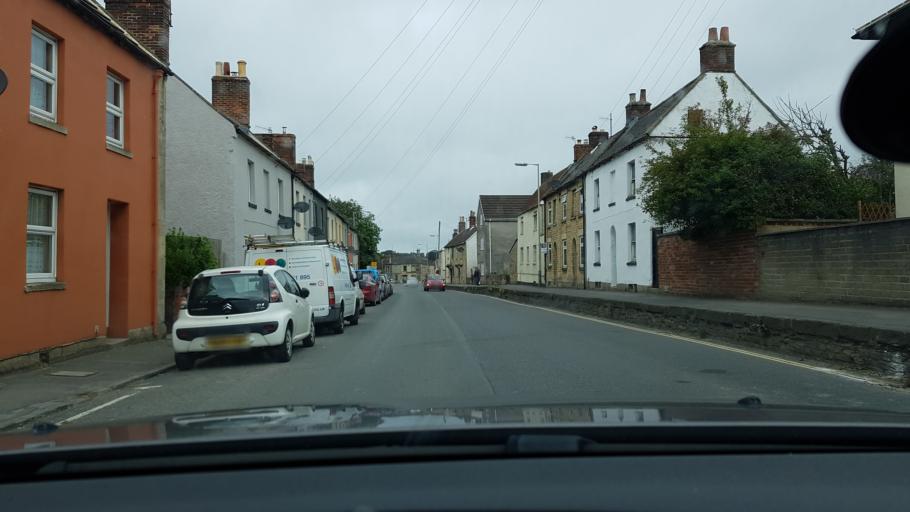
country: GB
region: England
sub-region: Wiltshire
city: Calne
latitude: 51.4339
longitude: -2.0013
